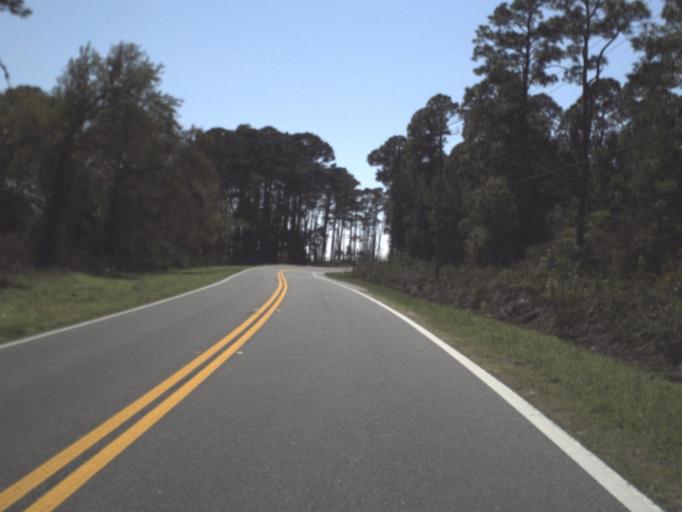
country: US
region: Florida
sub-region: Franklin County
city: Carrabelle
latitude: 29.8640
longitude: -84.6217
